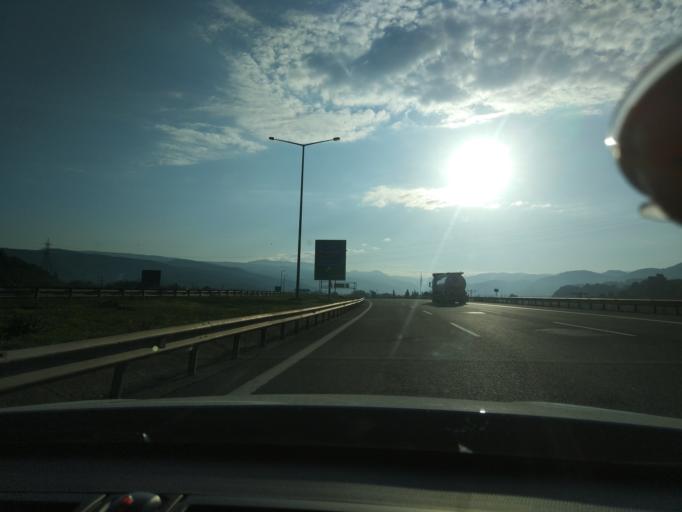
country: TR
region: Duzce
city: Kaynasli
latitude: 40.7855
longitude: 31.2654
